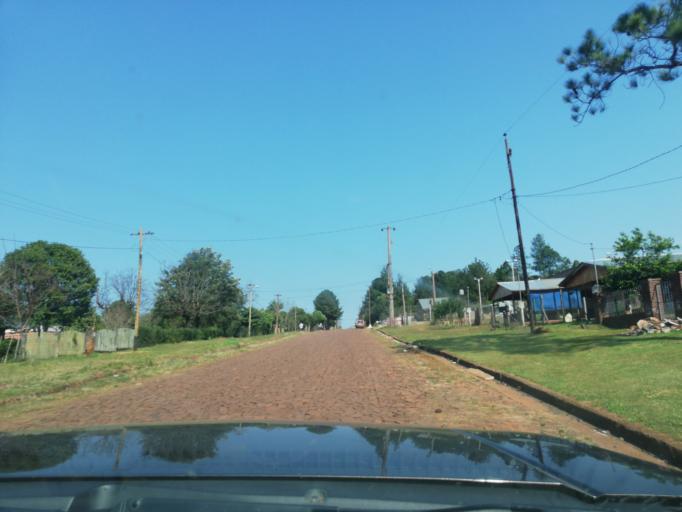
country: AR
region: Misiones
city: Bonpland
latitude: -27.4782
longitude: -55.4781
